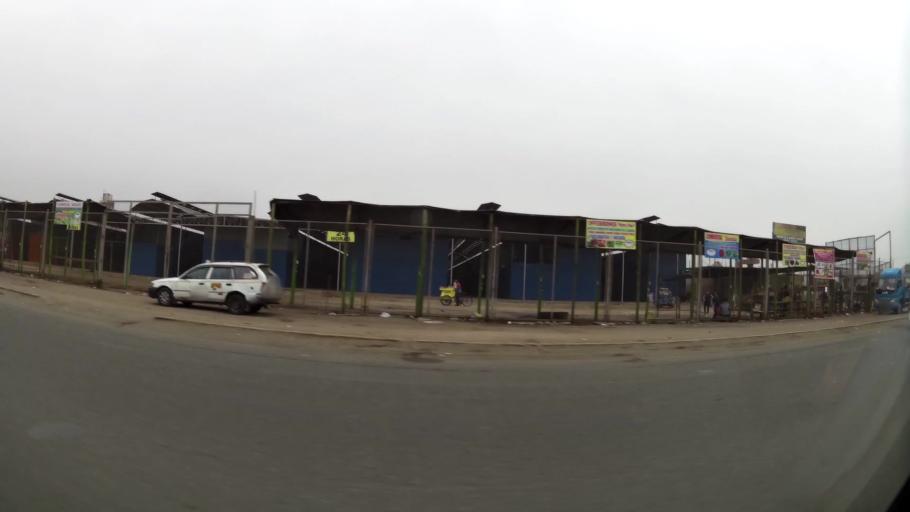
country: PE
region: Lima
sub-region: Lima
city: Independencia
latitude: -11.9375
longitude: -77.0690
